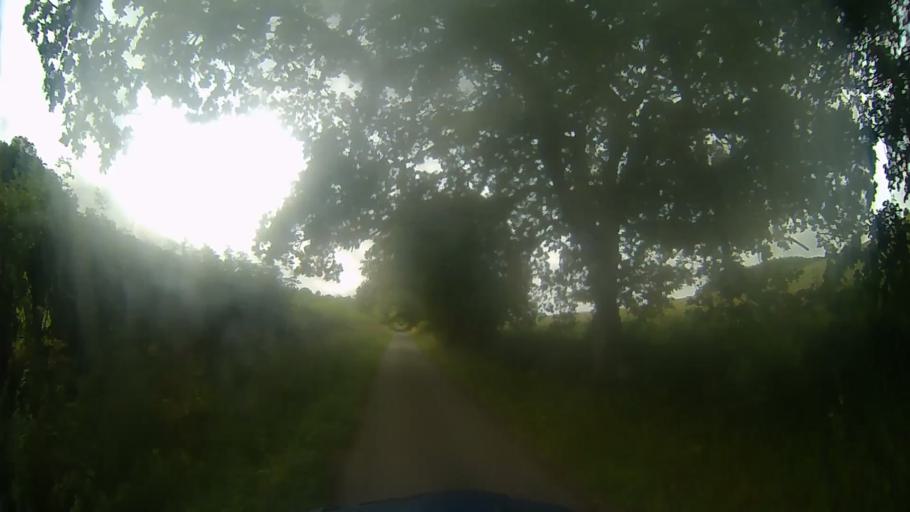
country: GB
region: England
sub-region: Hampshire
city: Overton
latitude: 51.2690
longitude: -1.3175
